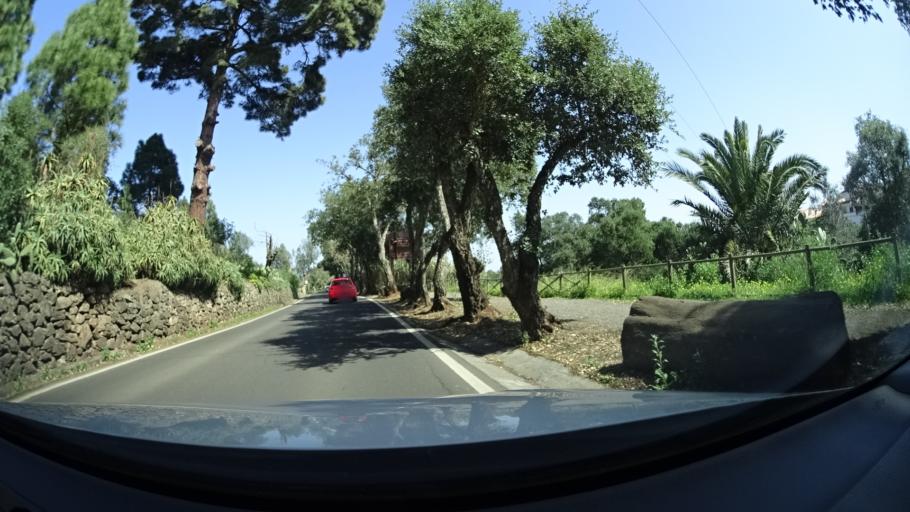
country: ES
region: Canary Islands
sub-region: Provincia de Las Palmas
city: Teror
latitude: 28.0686
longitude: -15.5417
